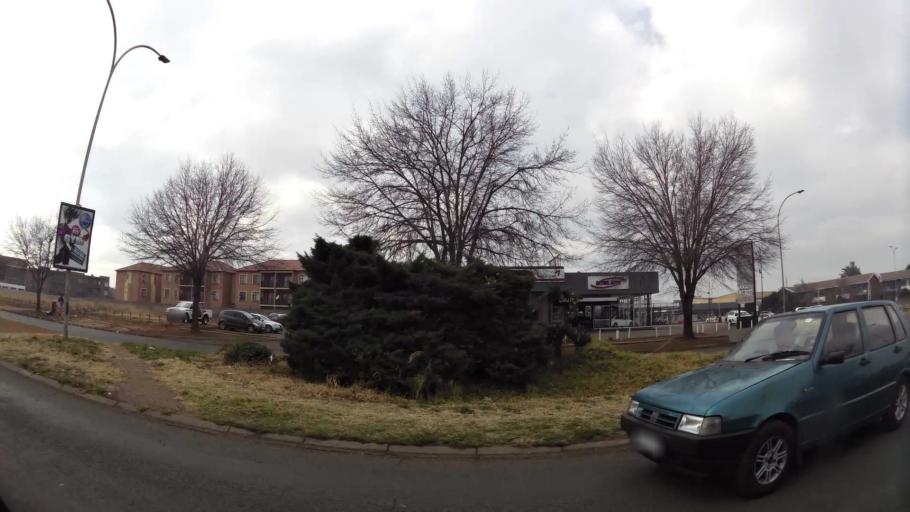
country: ZA
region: Gauteng
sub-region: Sedibeng District Municipality
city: Vanderbijlpark
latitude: -26.6972
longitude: 27.8323
